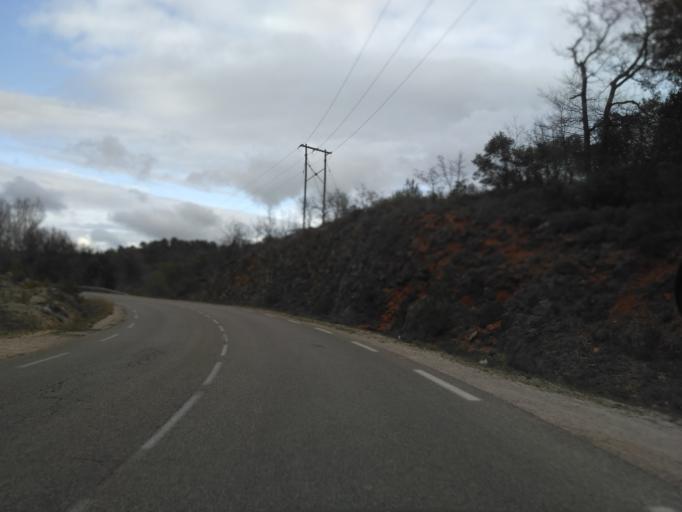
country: FR
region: Provence-Alpes-Cote d'Azur
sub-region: Departement du Var
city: Barjols
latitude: 43.5728
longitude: 6.0165
